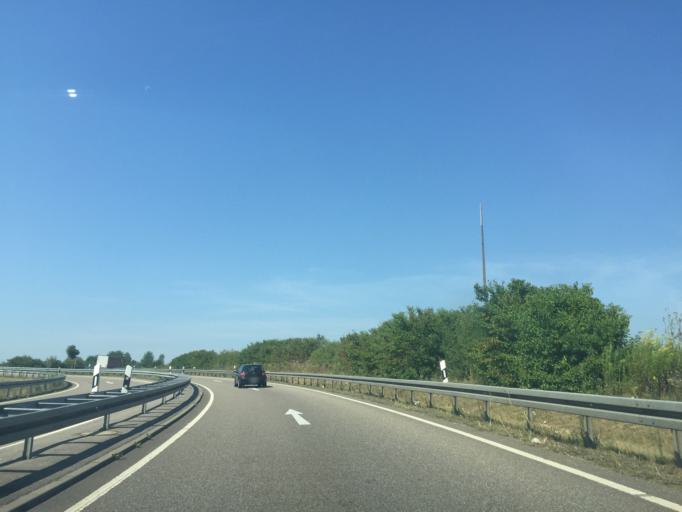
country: DE
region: Baden-Wuerttemberg
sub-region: Karlsruhe Region
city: Sinsheim
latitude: 49.2502
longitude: 8.8573
